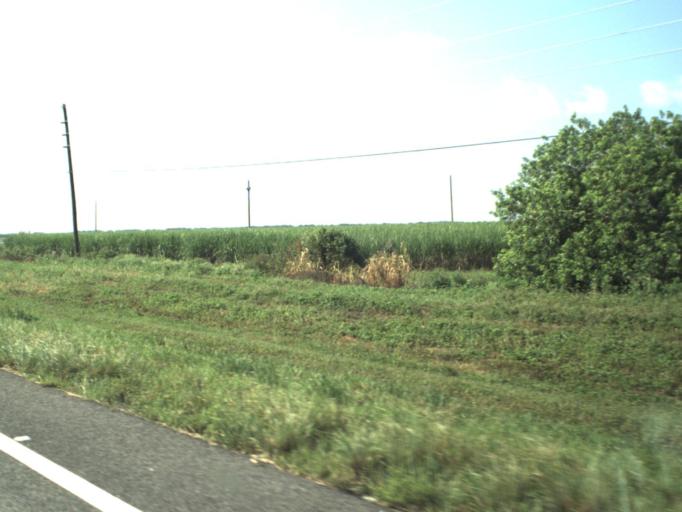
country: US
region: Florida
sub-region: Palm Beach County
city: Belle Glade Camp
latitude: 26.5059
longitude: -80.6705
